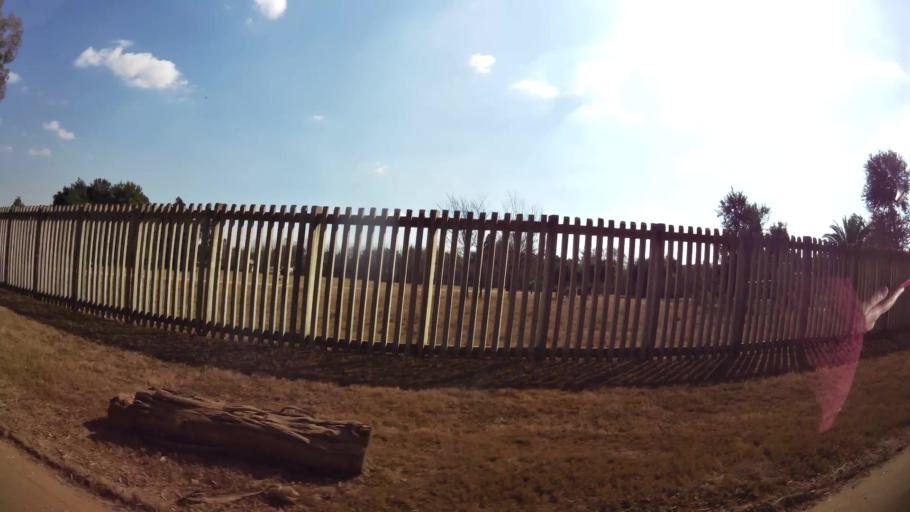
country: ZA
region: Gauteng
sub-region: Ekurhuleni Metropolitan Municipality
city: Benoni
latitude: -26.0886
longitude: 28.3278
